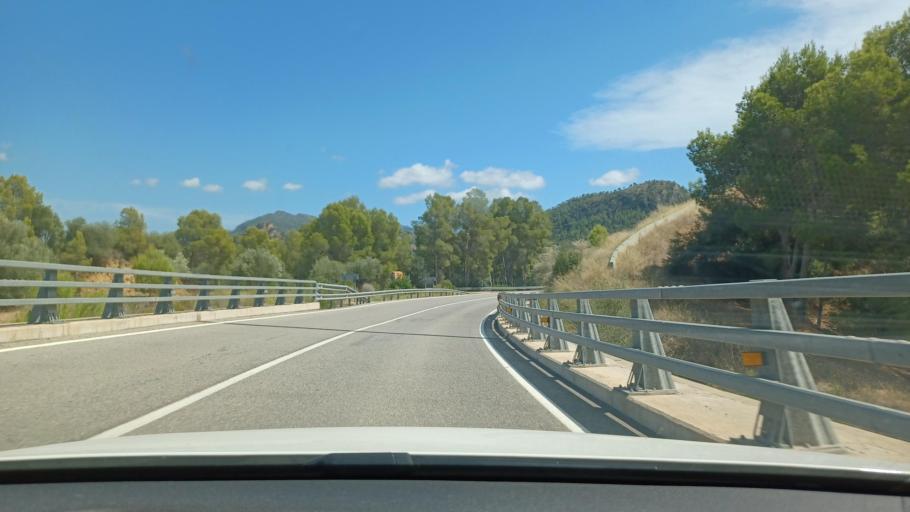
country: ES
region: Catalonia
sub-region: Provincia de Tarragona
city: Tivenys
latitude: 40.9344
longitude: 0.4776
